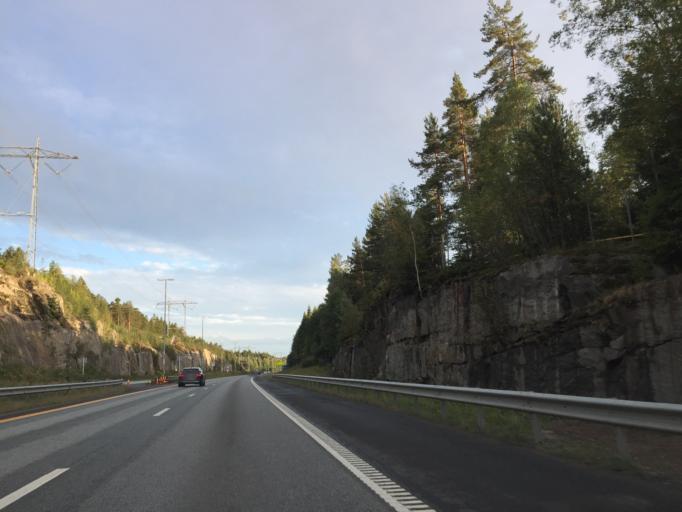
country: NO
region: Akershus
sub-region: Oppegard
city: Kolbotn
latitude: 59.8069
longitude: 10.8417
